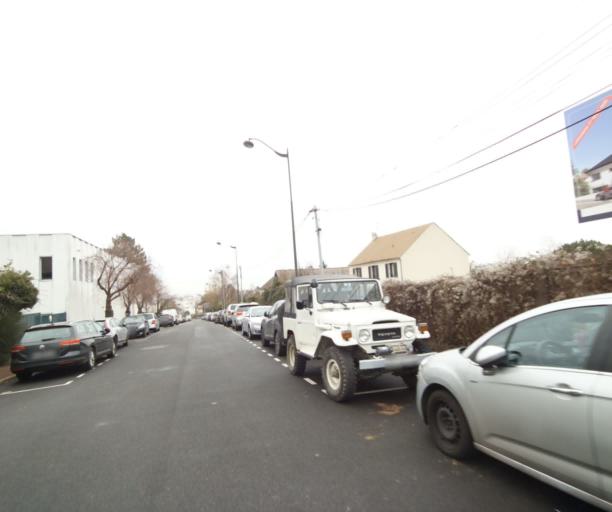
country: FR
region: Ile-de-France
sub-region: Departement des Hauts-de-Seine
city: Rueil-Malmaison
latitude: 48.8616
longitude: 2.1804
